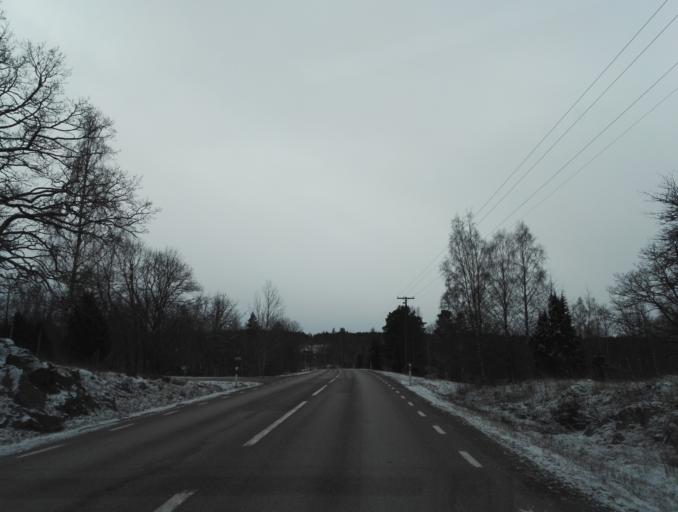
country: SE
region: Kalmar
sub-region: Hultsfreds Kommun
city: Virserum
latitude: 57.2920
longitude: 15.5658
